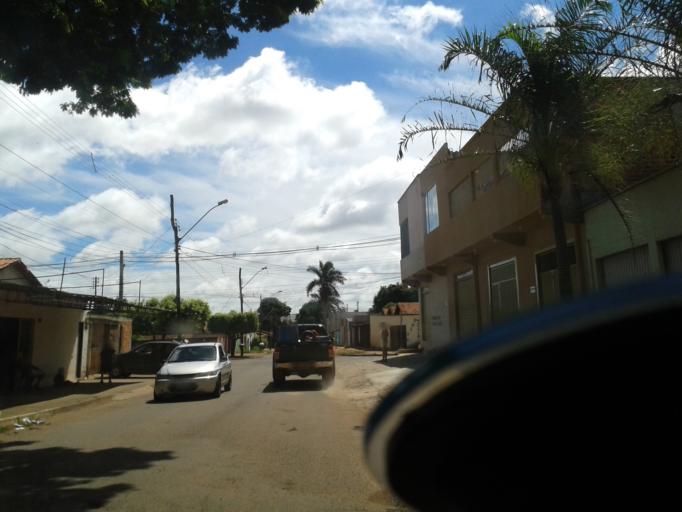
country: BR
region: Goias
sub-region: Goiania
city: Goiania
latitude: -16.6512
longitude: -49.3397
